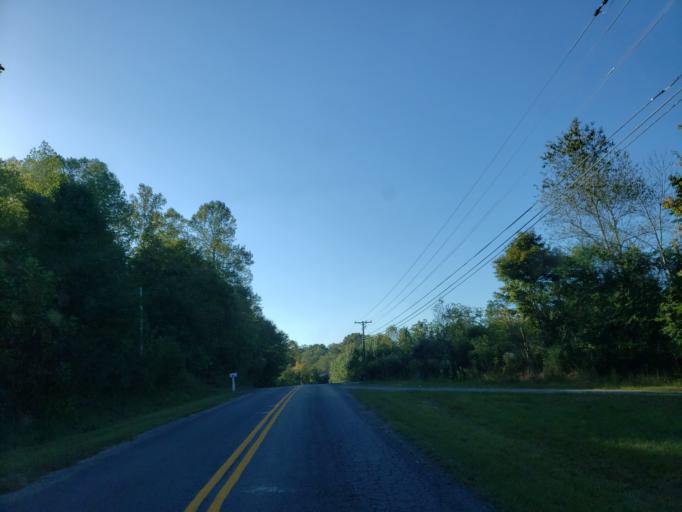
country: US
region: Georgia
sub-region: Pickens County
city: Nelson
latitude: 34.3859
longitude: -84.4054
